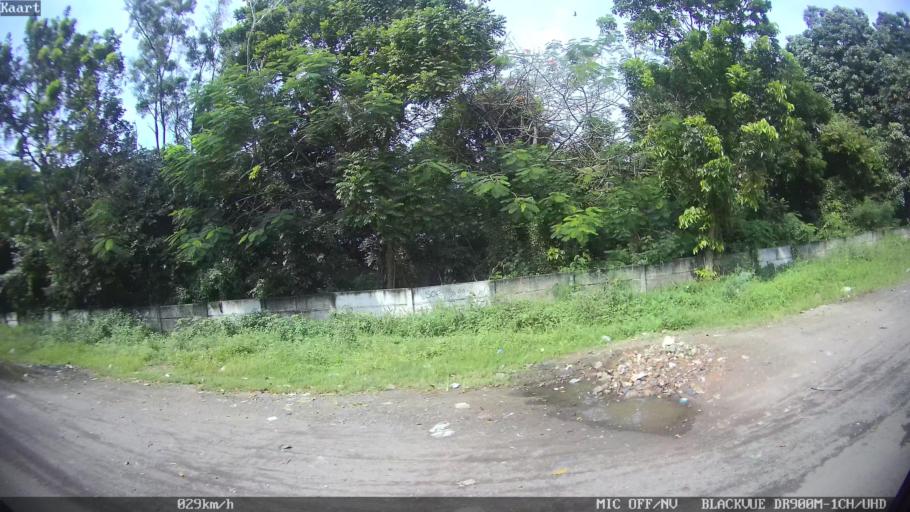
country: ID
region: Lampung
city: Kedaton
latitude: -5.3793
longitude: 105.2827
